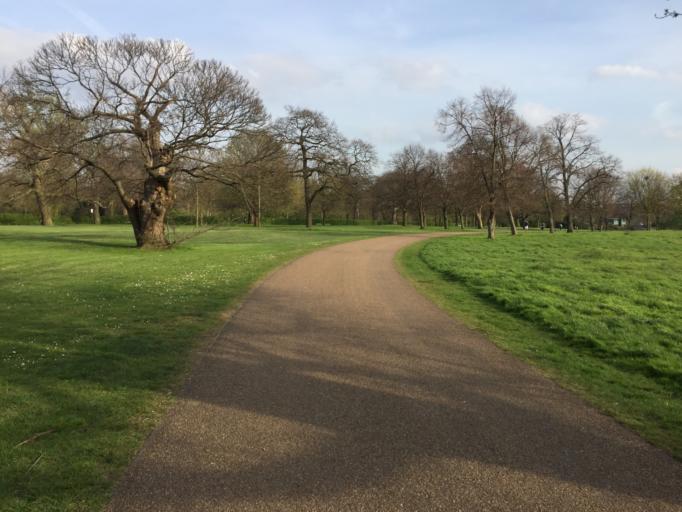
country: GB
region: England
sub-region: Greater London
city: Bayswater
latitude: 51.5101
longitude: -0.1718
